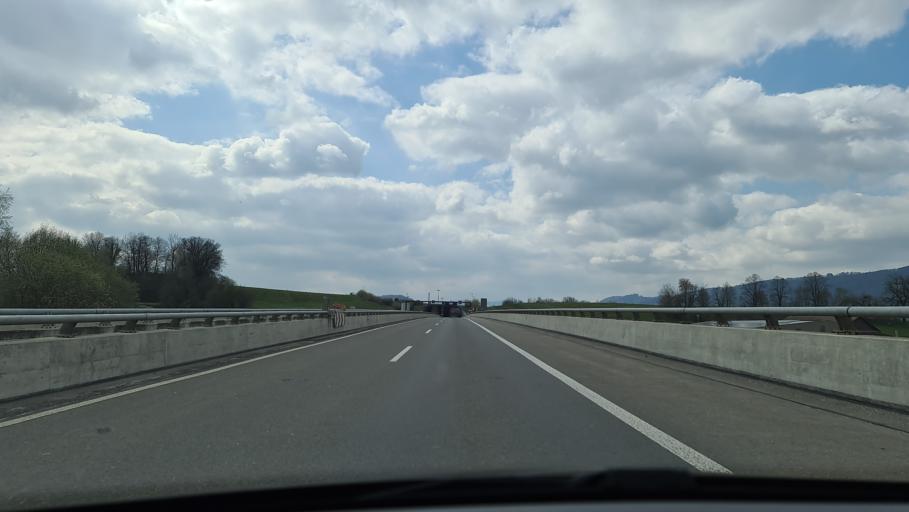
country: CH
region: Jura
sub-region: Delemont District
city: Courroux
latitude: 47.3518
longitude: 7.3619
